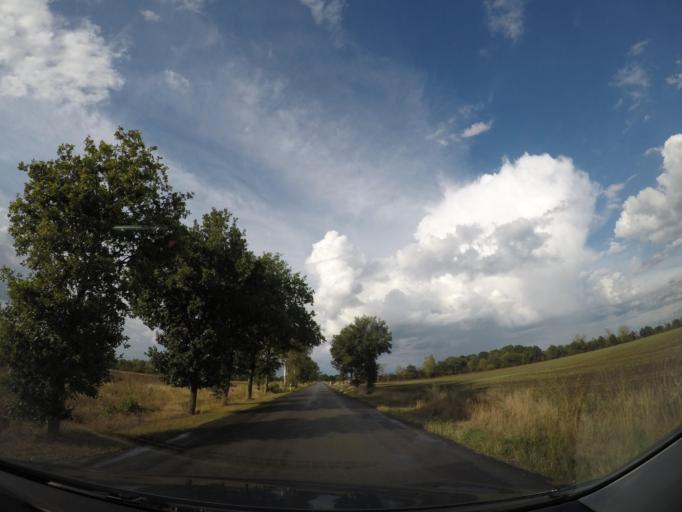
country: DE
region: Saxony-Anhalt
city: Mieste
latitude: 52.5237
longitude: 11.1488
